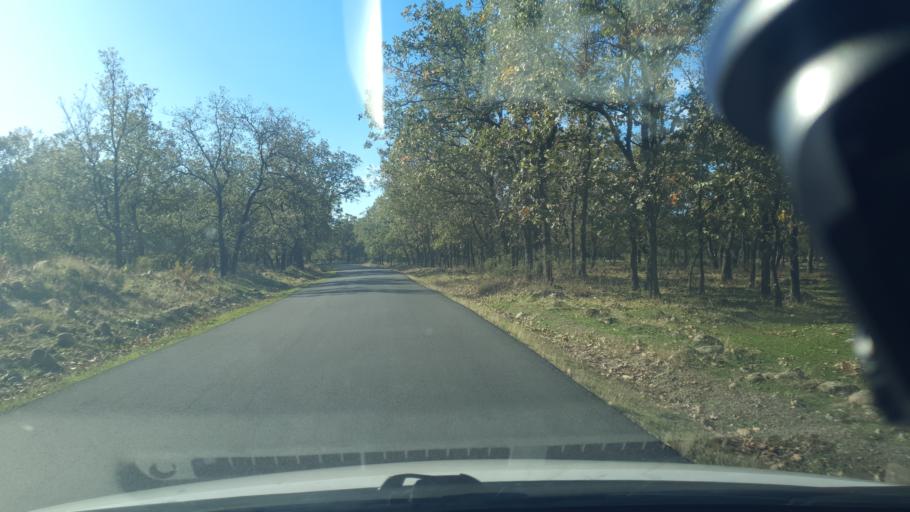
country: ES
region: Castille and Leon
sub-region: Provincia de Avila
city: Candeleda
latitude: 40.1333
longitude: -5.2640
